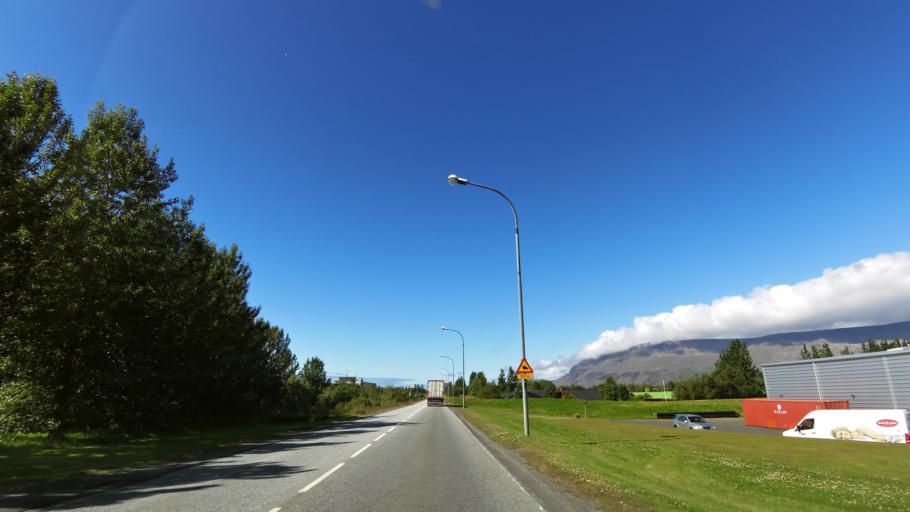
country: IS
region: Capital Region
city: Mosfellsbaer
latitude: 64.1612
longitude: -21.6823
